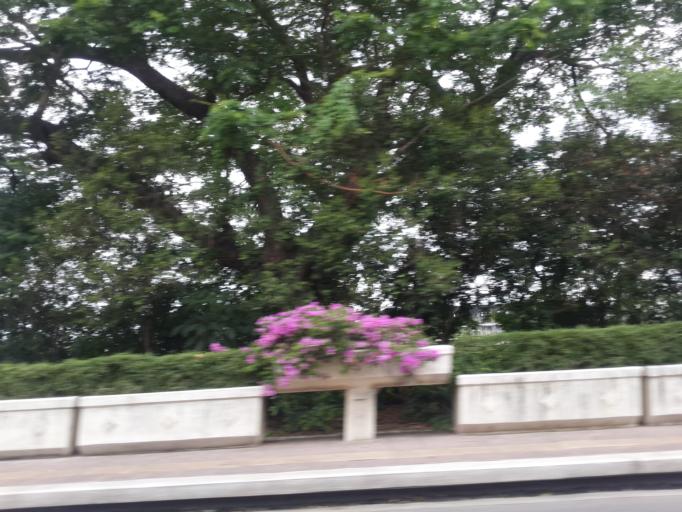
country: TH
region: Bangkok
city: Pom Prap Sattru Phai
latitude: 13.7649
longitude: 100.5185
